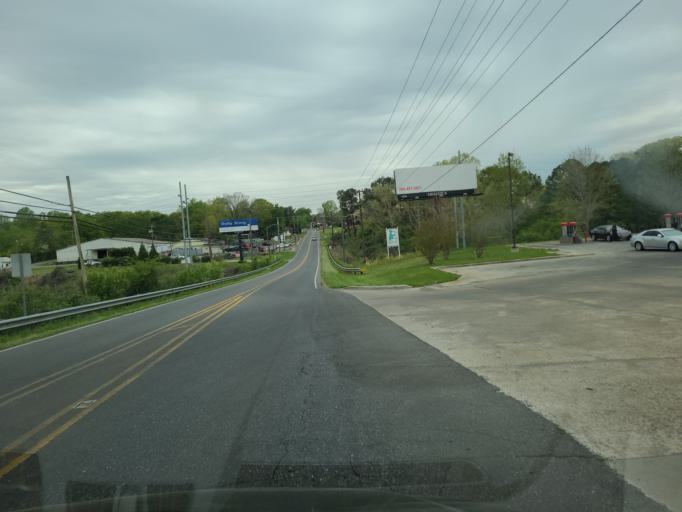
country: US
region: North Carolina
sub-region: Cleveland County
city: Shelby
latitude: 35.2959
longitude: -81.5160
